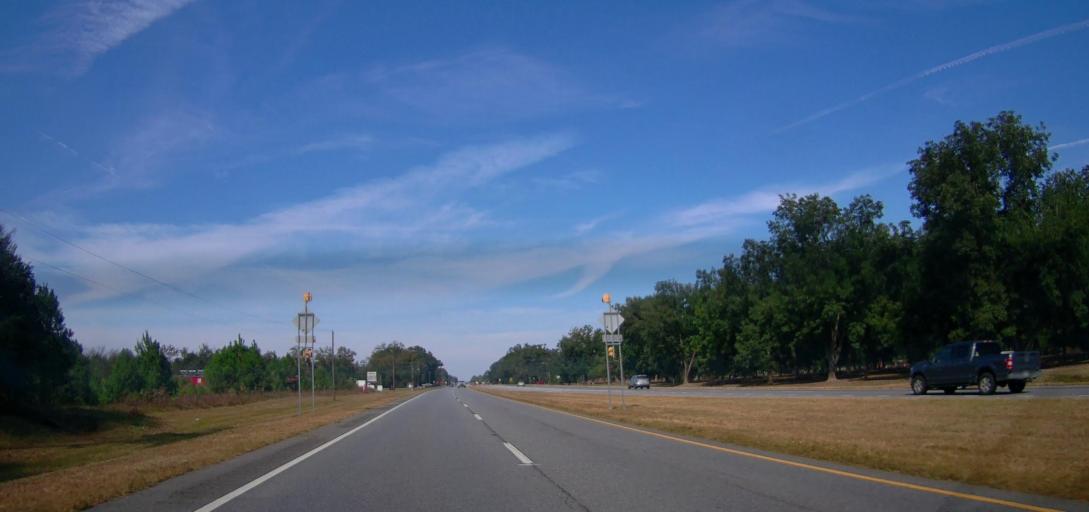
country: US
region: Georgia
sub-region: Dougherty County
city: Putney
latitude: 31.4674
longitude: -84.1180
